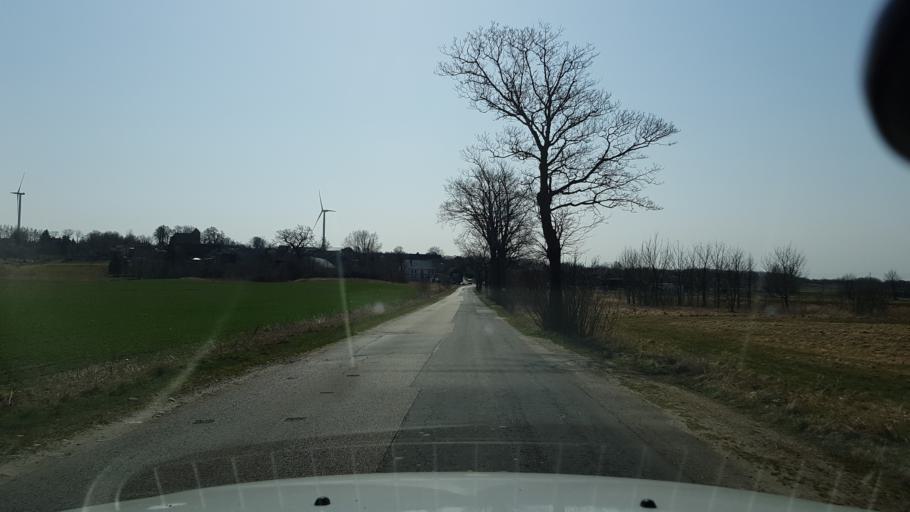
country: PL
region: West Pomeranian Voivodeship
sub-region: Powiat slawienski
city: Darlowo
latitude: 54.4840
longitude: 16.5086
